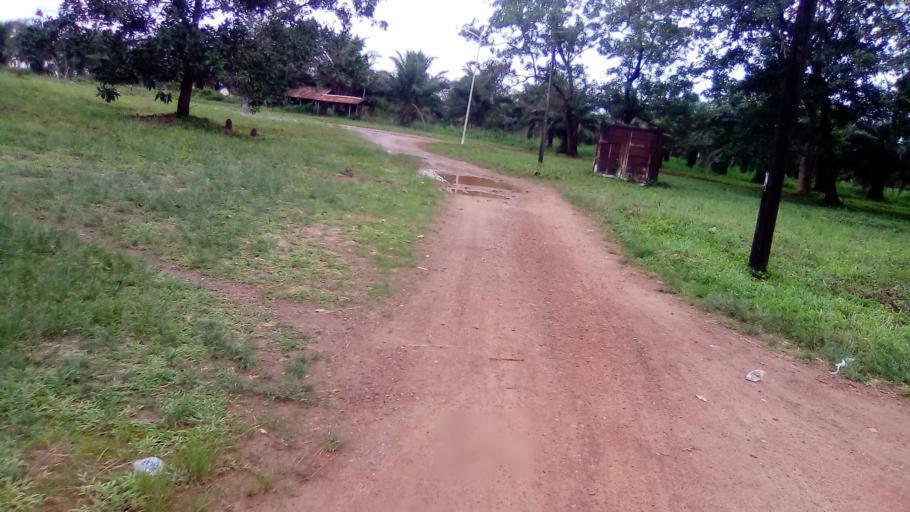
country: SL
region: Southern Province
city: Largo
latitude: 8.1173
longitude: -12.0677
